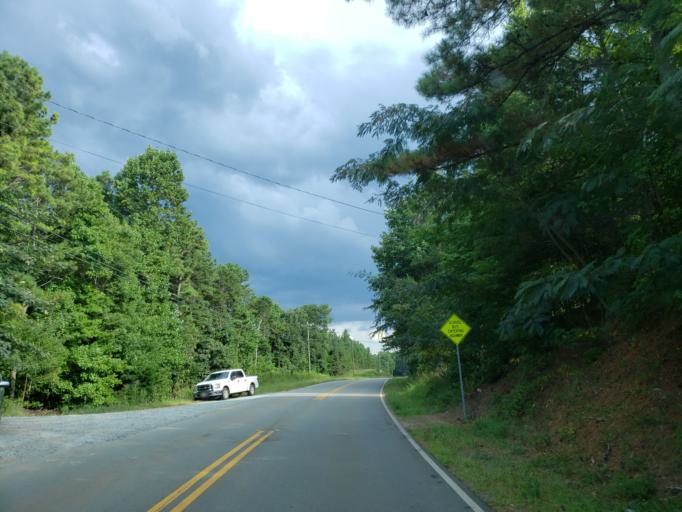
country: US
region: Georgia
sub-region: Pickens County
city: Jasper
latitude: 34.4062
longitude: -84.4804
